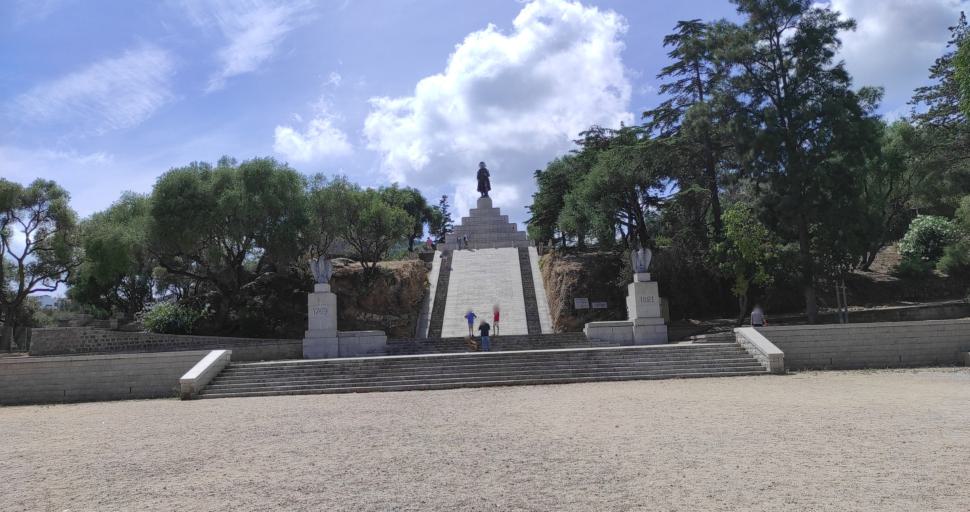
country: FR
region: Corsica
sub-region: Departement de la Corse-du-Sud
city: Ajaccio
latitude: 41.9166
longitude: 8.7244
